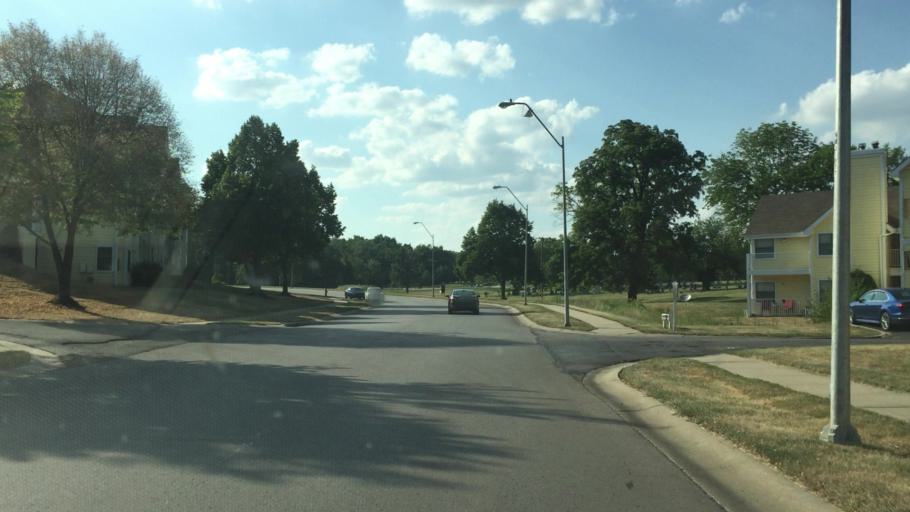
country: US
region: Missouri
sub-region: Clay County
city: Gladstone
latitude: 39.2433
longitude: -94.5966
